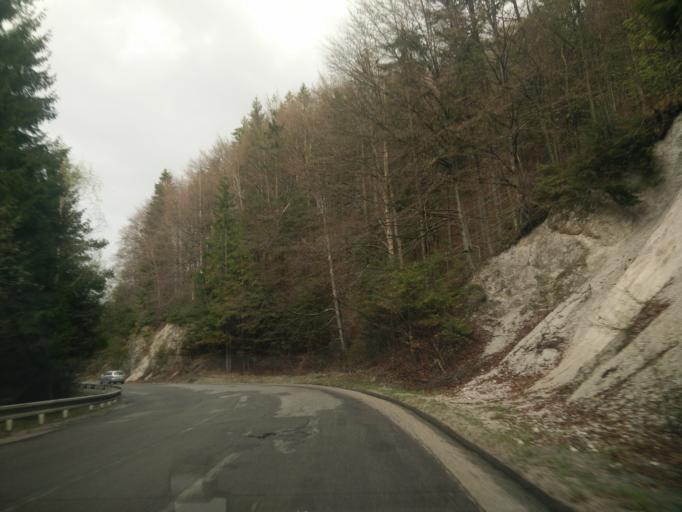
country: SK
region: Banskobystricky
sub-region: Okres Ziar nad Hronom
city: Kremnica
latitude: 48.8359
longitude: 18.9700
